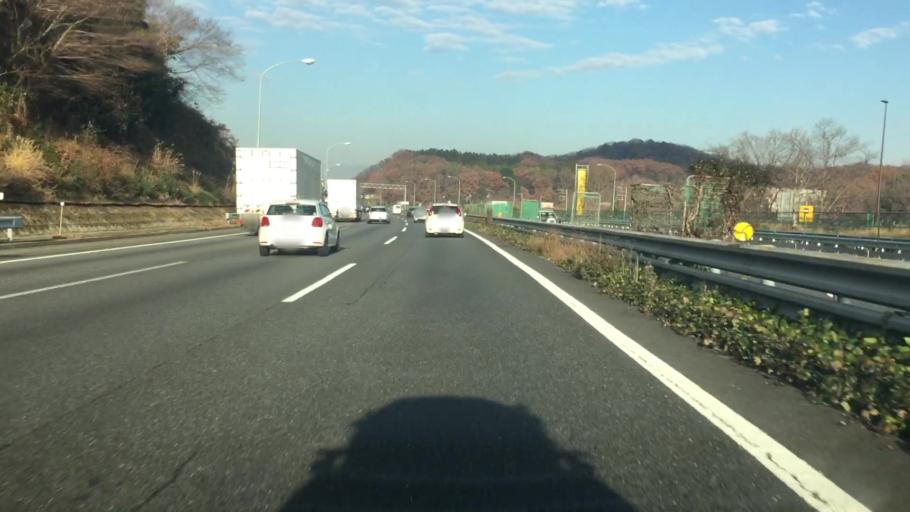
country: JP
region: Saitama
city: Ogawa
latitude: 36.0827
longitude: 139.2967
